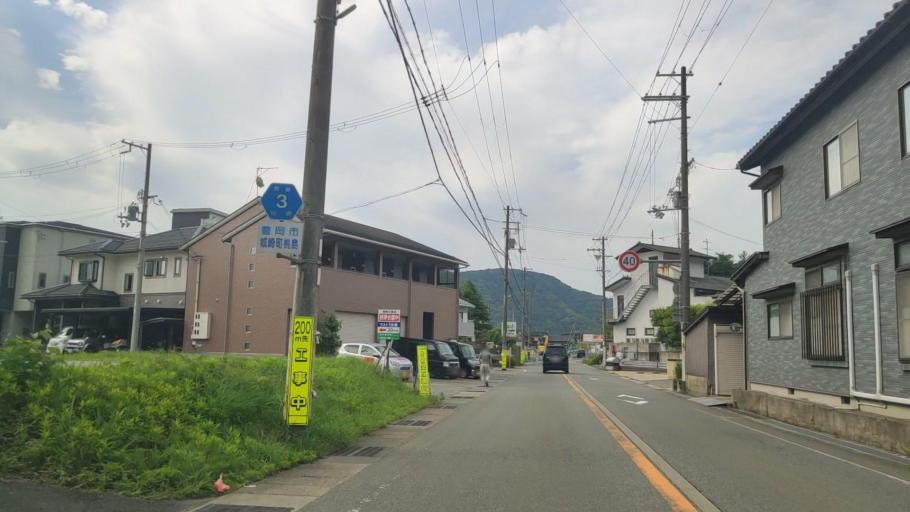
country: JP
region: Hyogo
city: Toyooka
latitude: 35.6311
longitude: 134.8163
